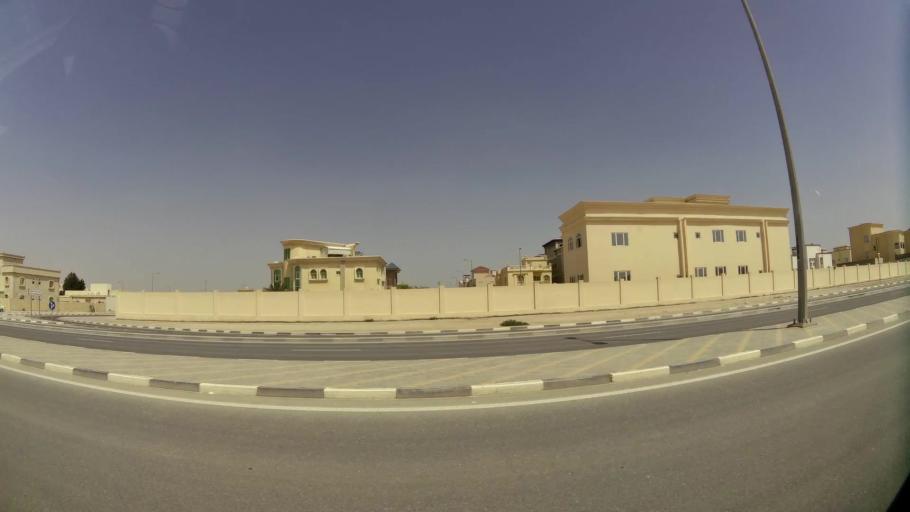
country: QA
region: Baladiyat Umm Salal
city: Umm Salal Muhammad
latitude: 25.3823
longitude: 51.4564
